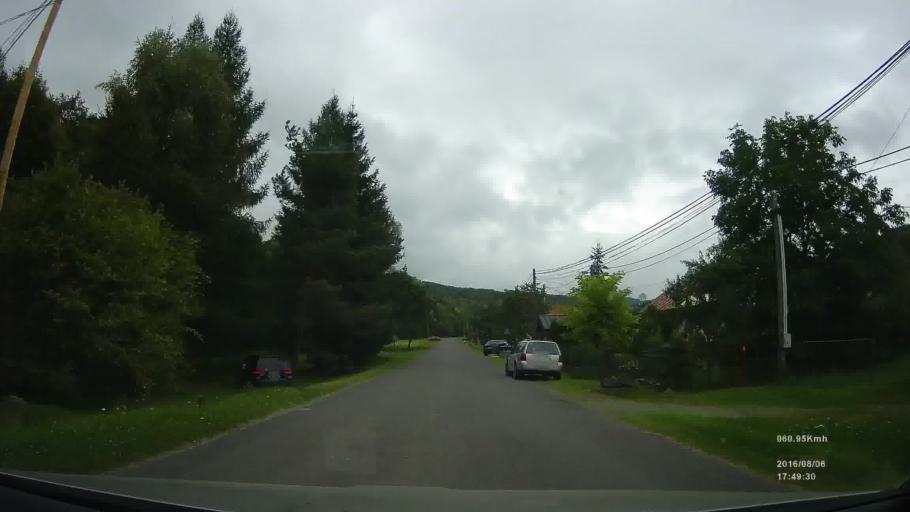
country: SK
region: Presovsky
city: Svidnik
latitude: 49.3839
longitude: 21.5690
